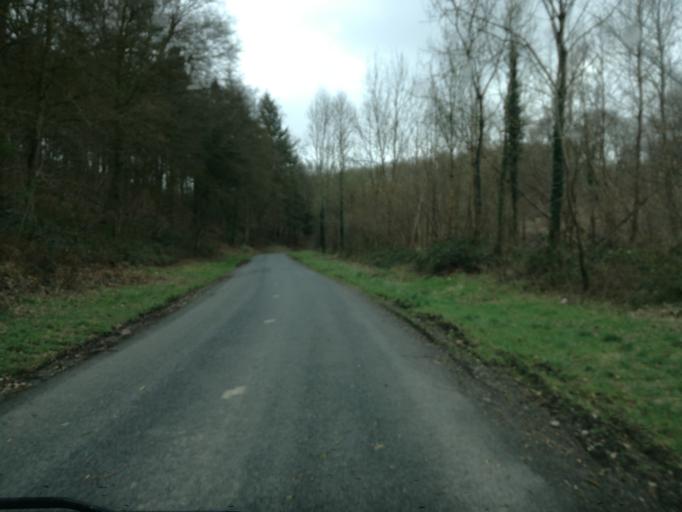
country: FR
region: Haute-Normandie
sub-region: Departement de la Seine-Maritime
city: Auzebosc
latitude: 49.5608
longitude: 0.7400
